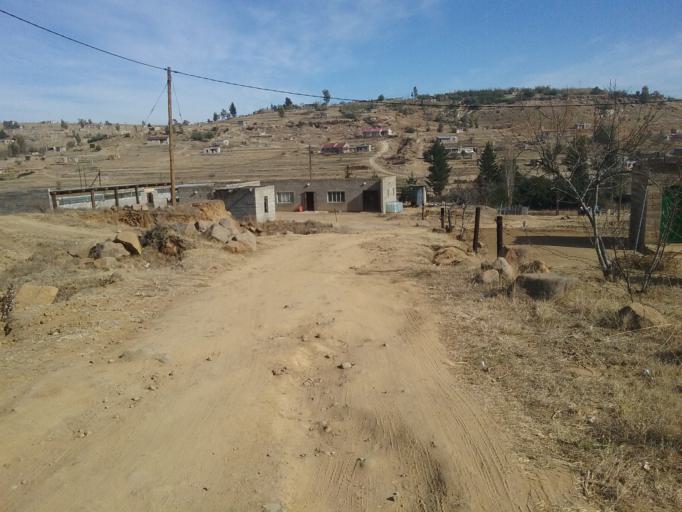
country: LS
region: Maseru
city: Maseru
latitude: -29.4180
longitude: 27.5512
